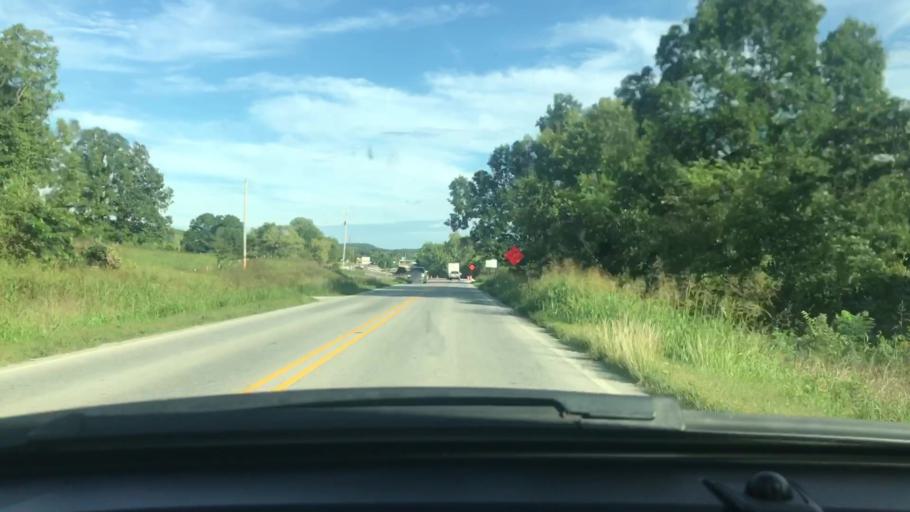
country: US
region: Arkansas
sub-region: Sharp County
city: Cherokee Village
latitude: 36.3057
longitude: -91.4519
